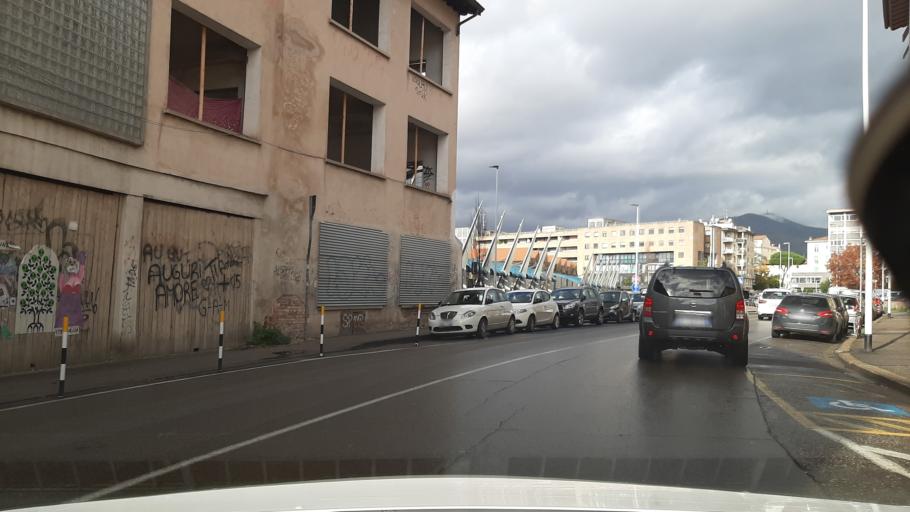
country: IT
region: Tuscany
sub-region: Province of Florence
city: Florence
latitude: 43.7951
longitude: 11.2446
